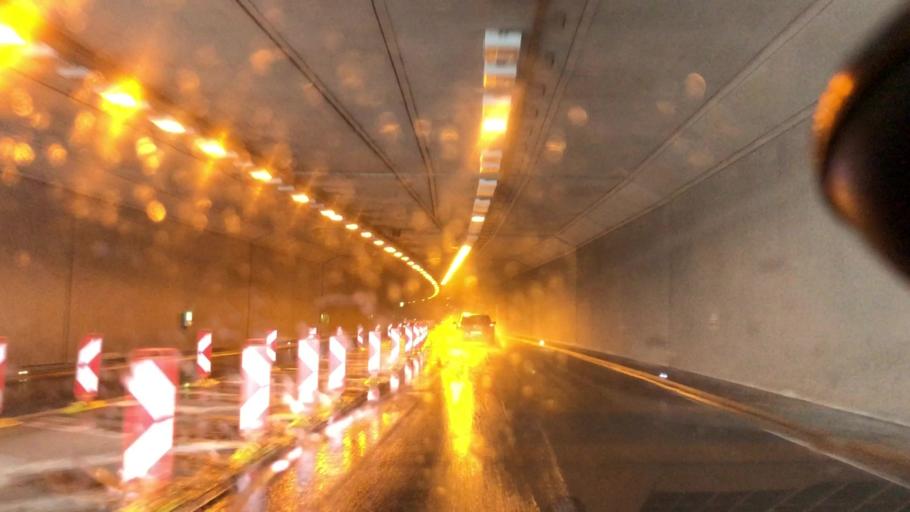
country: DE
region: North Rhine-Westphalia
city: Porta Westfalica
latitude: 52.2450
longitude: 8.9163
